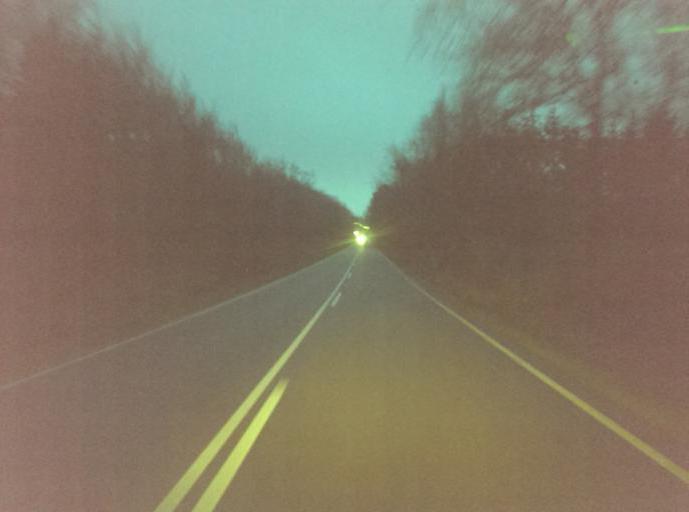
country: DK
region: South Denmark
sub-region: Esbjerg Kommune
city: Tjaereborg
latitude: 55.4816
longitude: 8.5793
